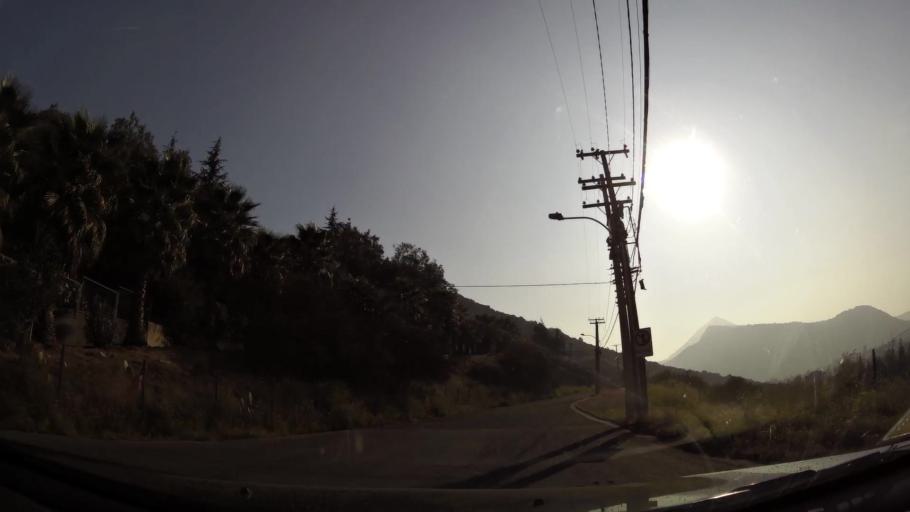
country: CL
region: Santiago Metropolitan
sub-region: Provincia de Santiago
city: Villa Presidente Frei, Nunoa, Santiago, Chile
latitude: -33.3677
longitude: -70.5306
